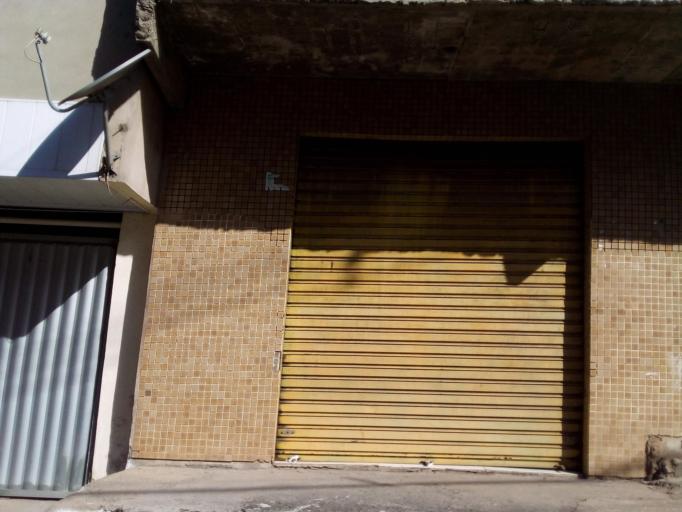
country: BR
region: Espirito Santo
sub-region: Vitoria
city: Vitoria
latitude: -20.3085
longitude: -40.3734
